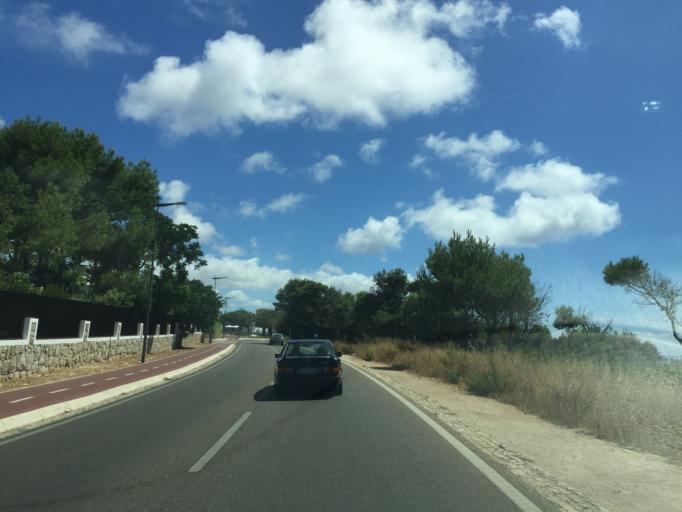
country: PT
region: Lisbon
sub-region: Cascais
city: Cascais
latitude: 38.6955
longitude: -9.4505
